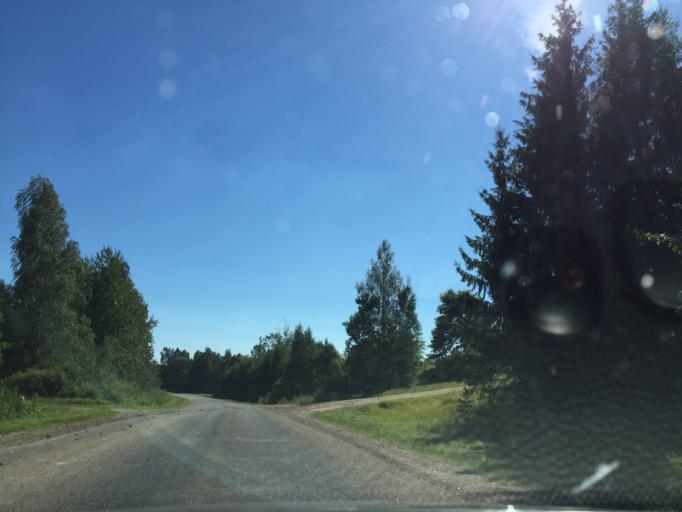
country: LV
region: Akniste
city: Akniste
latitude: 56.0398
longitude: 25.9082
